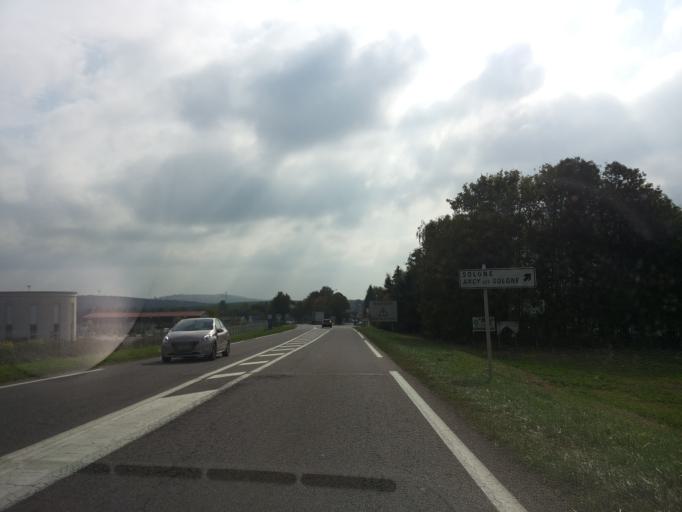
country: FR
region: Lorraine
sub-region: Departement de la Moselle
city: Solgne
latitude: 48.9724
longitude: 6.2949
